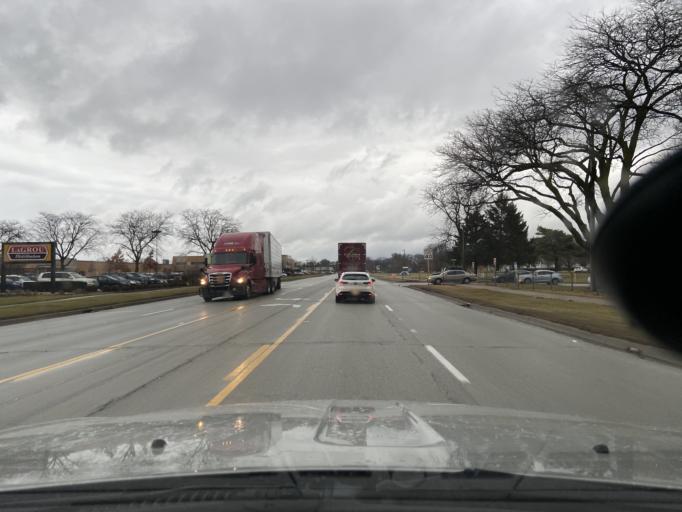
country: US
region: Illinois
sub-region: Cook County
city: Des Plaines
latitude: 42.0192
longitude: -87.9090
